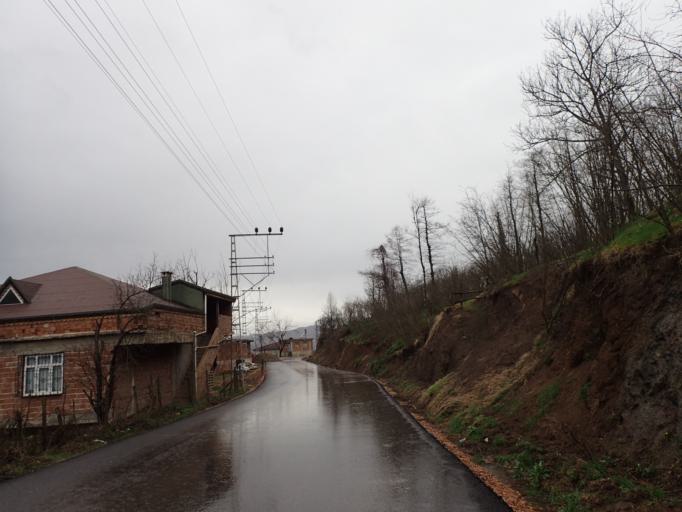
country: TR
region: Ordu
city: Camas
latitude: 40.8805
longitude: 37.4980
